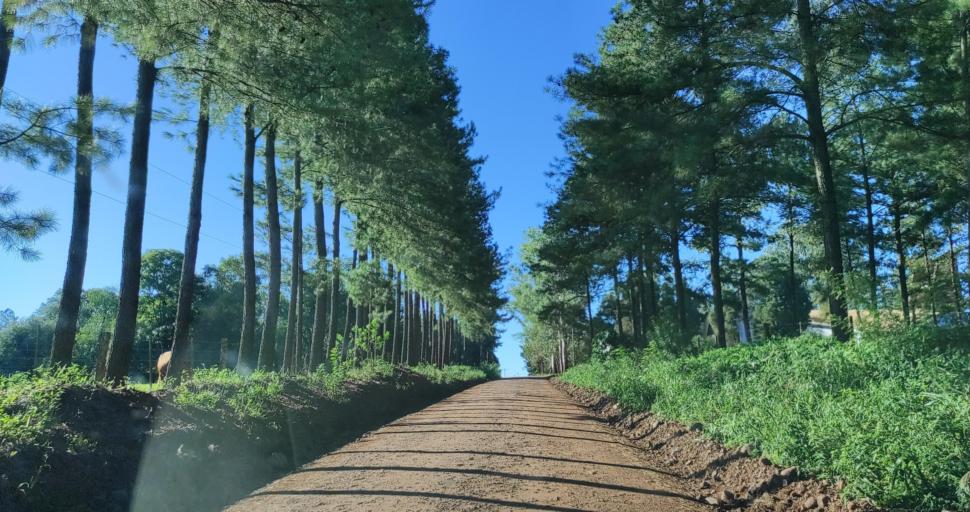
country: AR
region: Misiones
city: Garuhape
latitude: -26.8679
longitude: -54.9950
